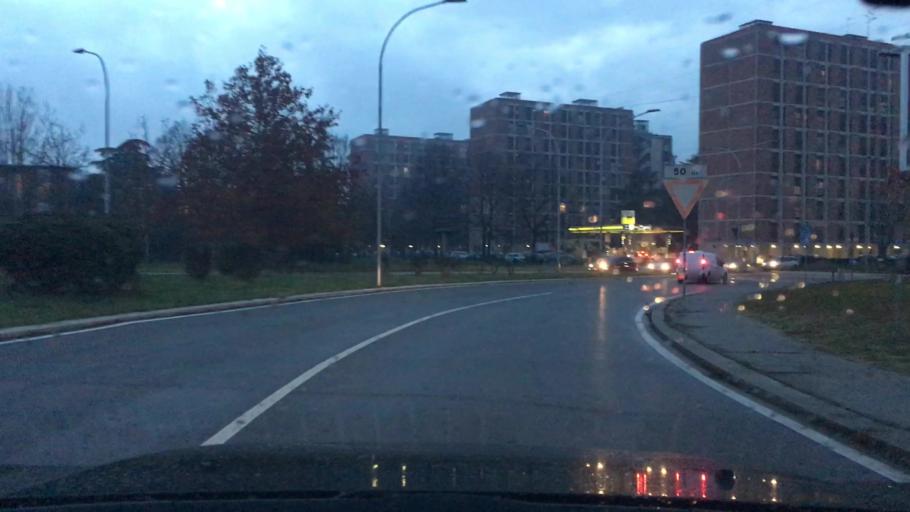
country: IT
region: Emilia-Romagna
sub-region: Provincia di Bologna
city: Casalecchio di Reno
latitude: 44.4928
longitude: 11.2882
